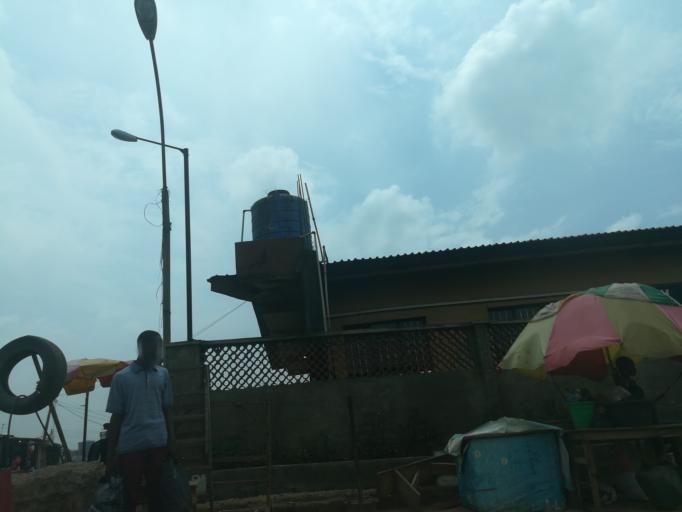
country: NG
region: Lagos
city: Ikorodu
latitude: 6.6094
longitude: 3.5057
